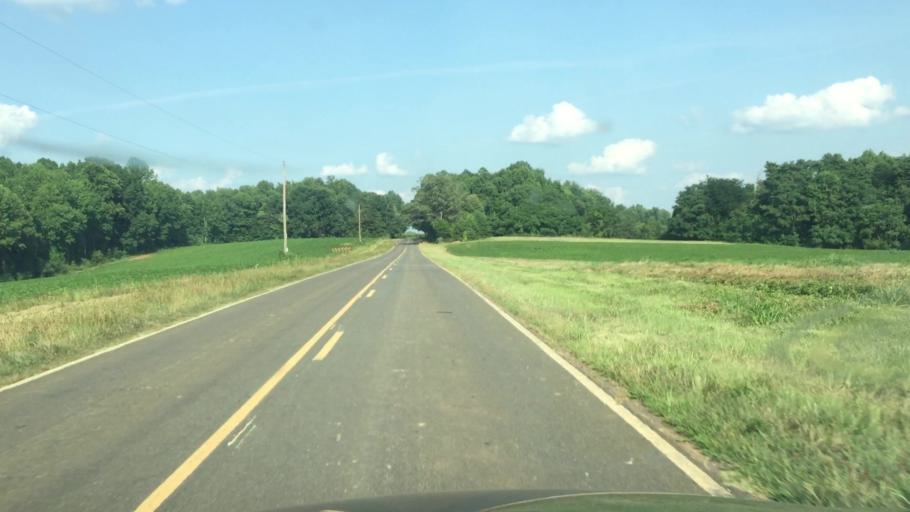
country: US
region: North Carolina
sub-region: Rockingham County
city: Reidsville
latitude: 36.2745
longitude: -79.5738
